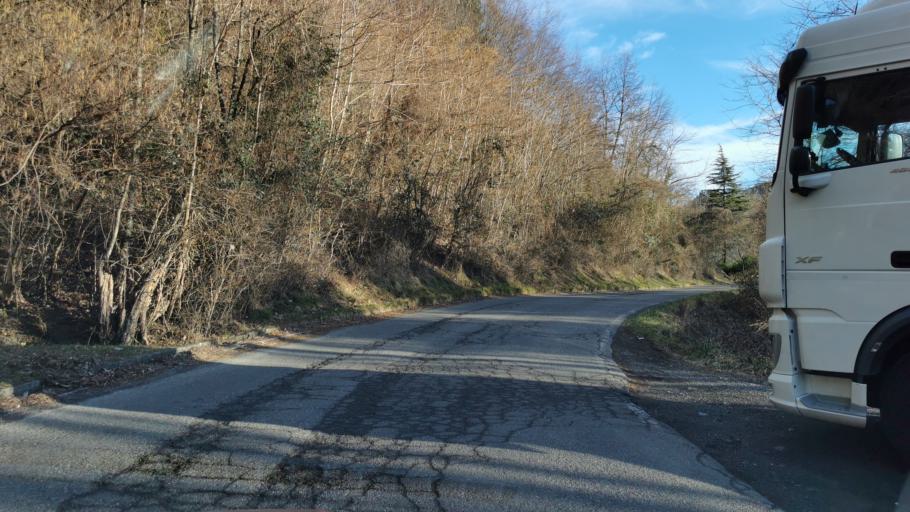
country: IT
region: Lombardy
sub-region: Provincia di Como
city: Plesio
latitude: 46.0430
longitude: 9.2248
